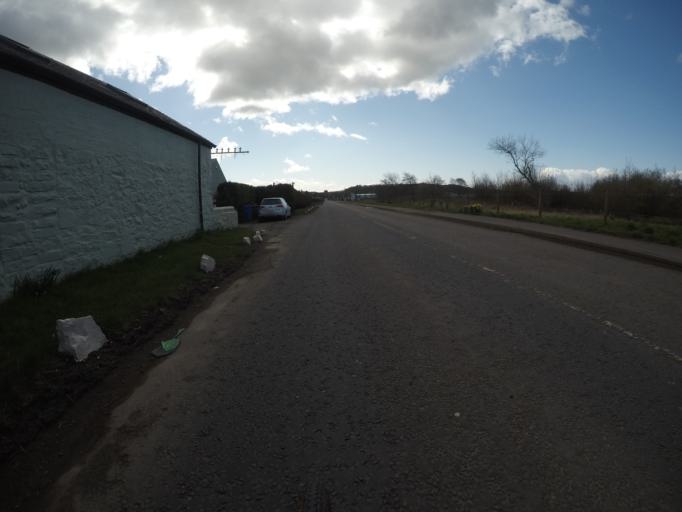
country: GB
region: Scotland
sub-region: North Ayrshire
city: Dreghorn
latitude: 55.5896
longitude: -4.6016
